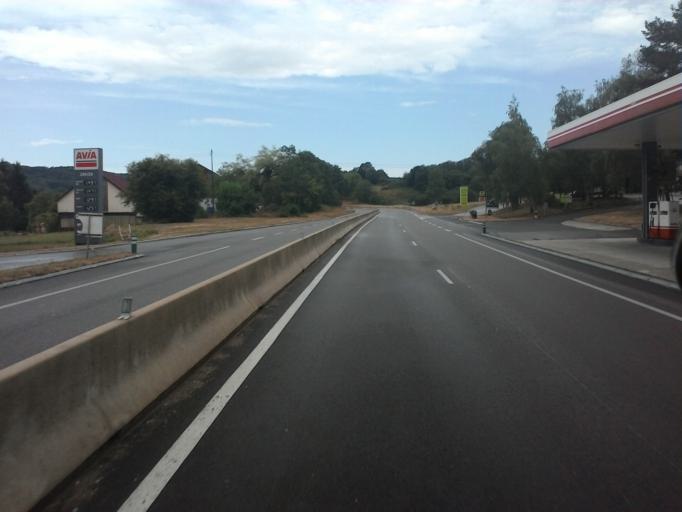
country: FR
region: Franche-Comte
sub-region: Departement du Jura
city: Poligny
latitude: 46.8074
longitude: 5.5813
